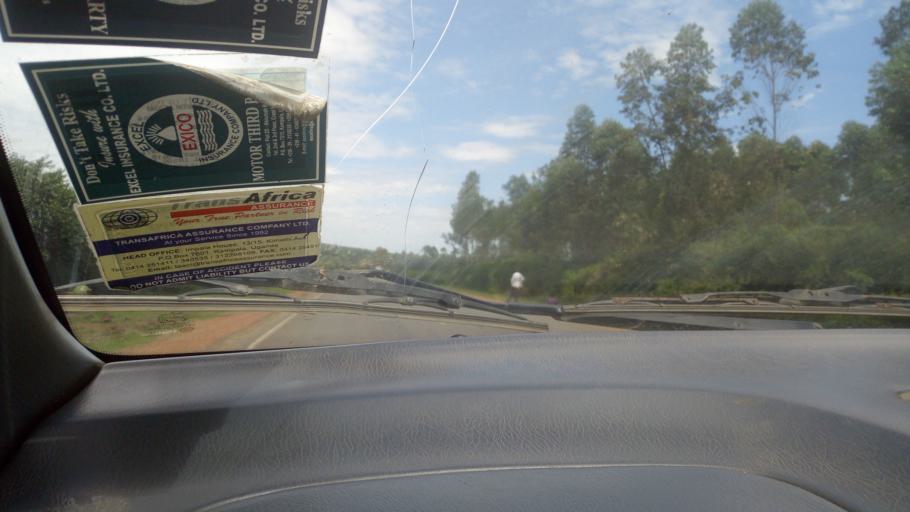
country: UG
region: Western Region
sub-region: Mbarara District
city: Bwizibwera
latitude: -0.3666
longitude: 30.5653
